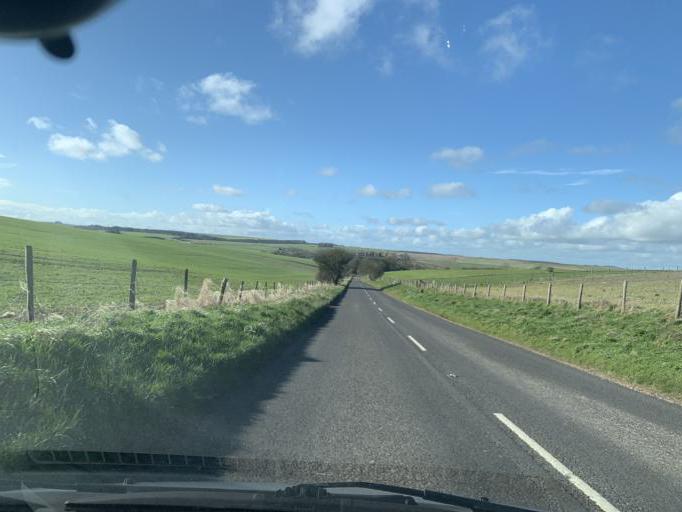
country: GB
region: England
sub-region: Wiltshire
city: Stockton
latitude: 51.1896
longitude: -2.0017
